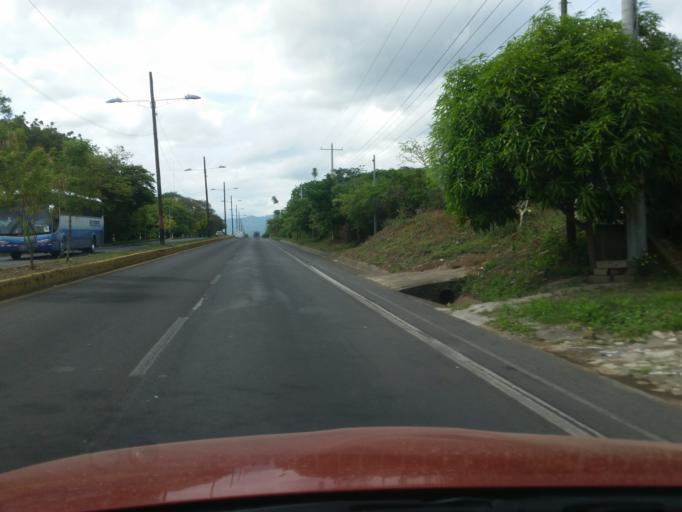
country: NI
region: Masaya
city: Nindiri
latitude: 12.0091
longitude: -86.1386
